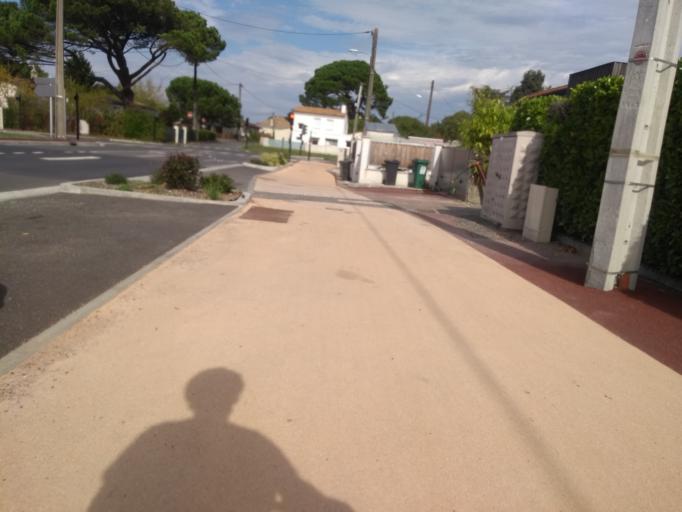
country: FR
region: Aquitaine
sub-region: Departement de la Gironde
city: Gradignan
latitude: 44.7756
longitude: -0.6214
